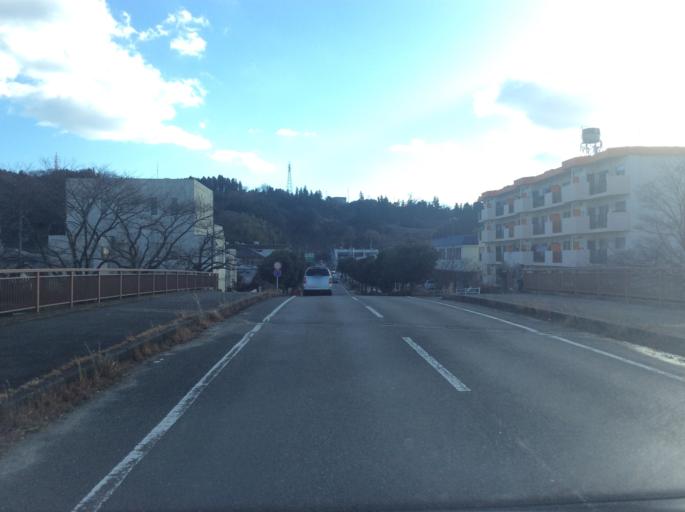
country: JP
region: Fukushima
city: Iwaki
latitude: 37.0499
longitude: 140.8848
